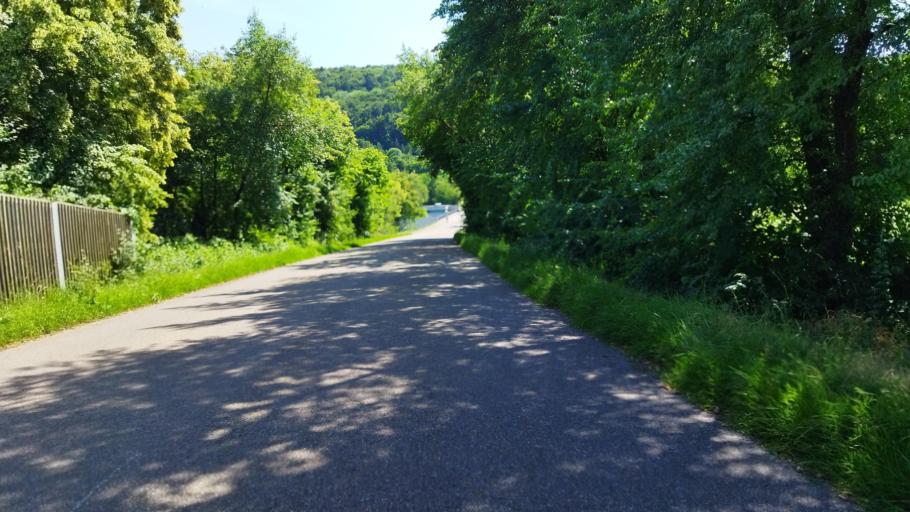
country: DE
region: Bavaria
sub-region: Lower Bavaria
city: Ihrlerstein
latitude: 48.9257
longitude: 11.8518
